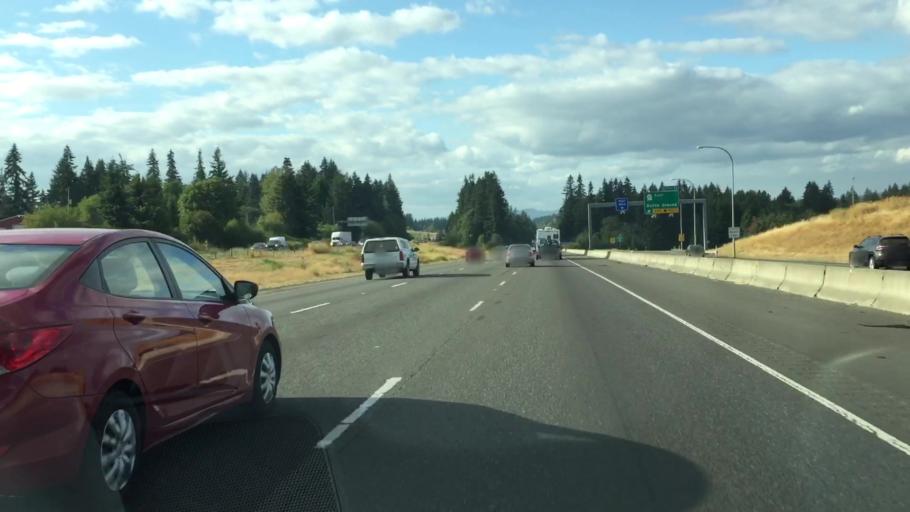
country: US
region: Washington
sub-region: Clark County
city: Mount Vista
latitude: 45.7702
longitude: -122.6690
